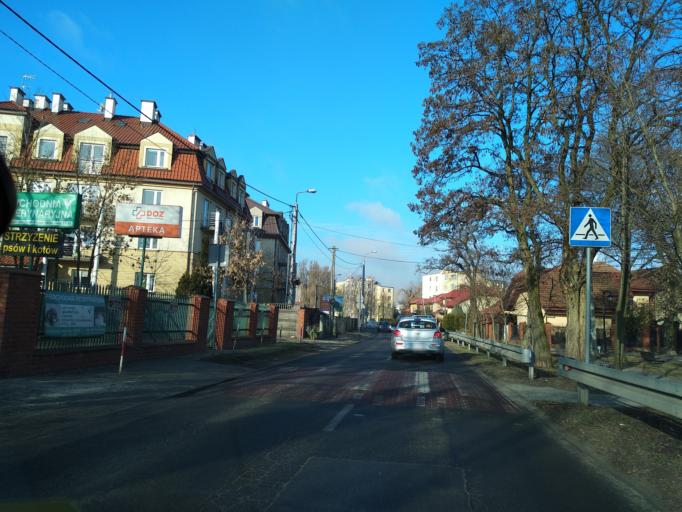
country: PL
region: Masovian Voivodeship
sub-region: Powiat piaseczynski
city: Mysiadlo
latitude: 52.0968
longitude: 21.0156
